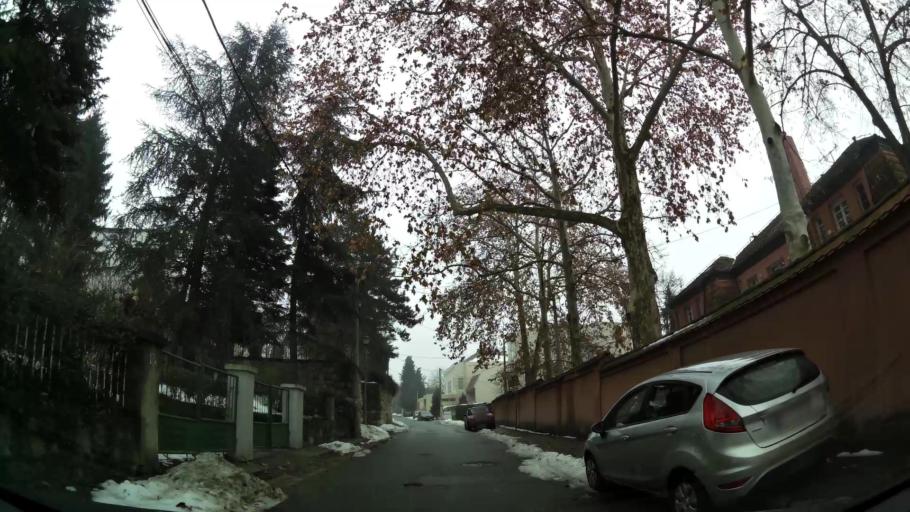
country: RS
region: Central Serbia
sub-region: Belgrade
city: Savski Venac
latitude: 44.7853
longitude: 20.4472
